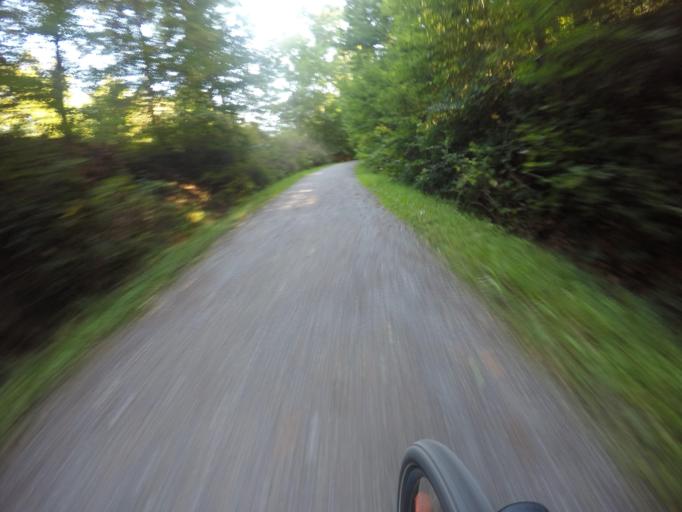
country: DE
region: Baden-Wuerttemberg
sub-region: Regierungsbezirk Stuttgart
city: Stuttgart
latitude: 48.7551
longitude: 9.1239
